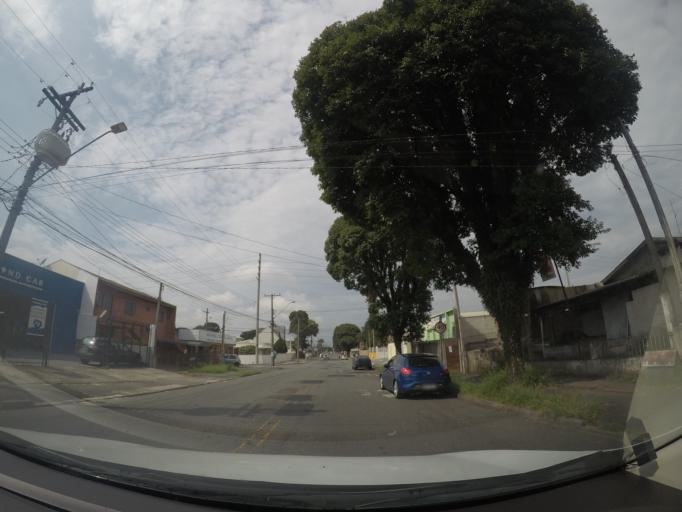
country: BR
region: Parana
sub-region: Sao Jose Dos Pinhais
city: Sao Jose dos Pinhais
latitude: -25.5106
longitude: -49.2832
